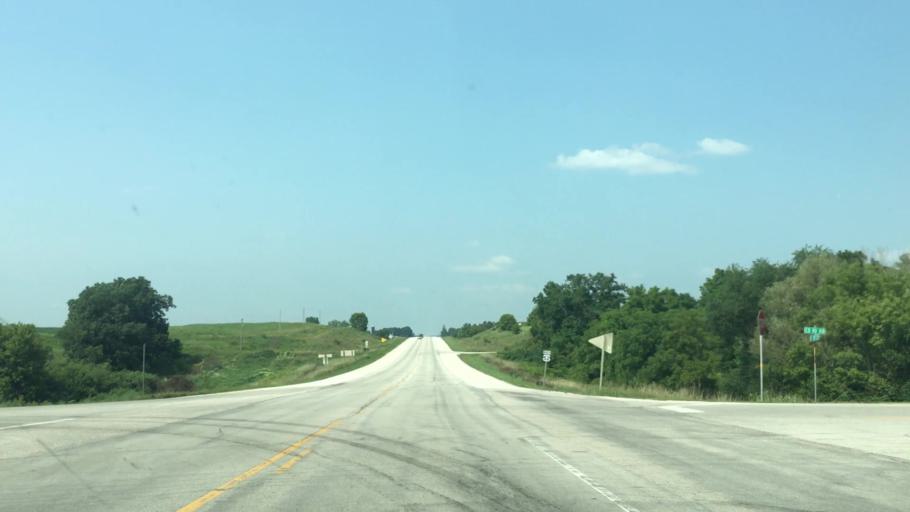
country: US
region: Minnesota
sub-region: Fillmore County
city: Harmony
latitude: 43.4573
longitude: -91.8696
